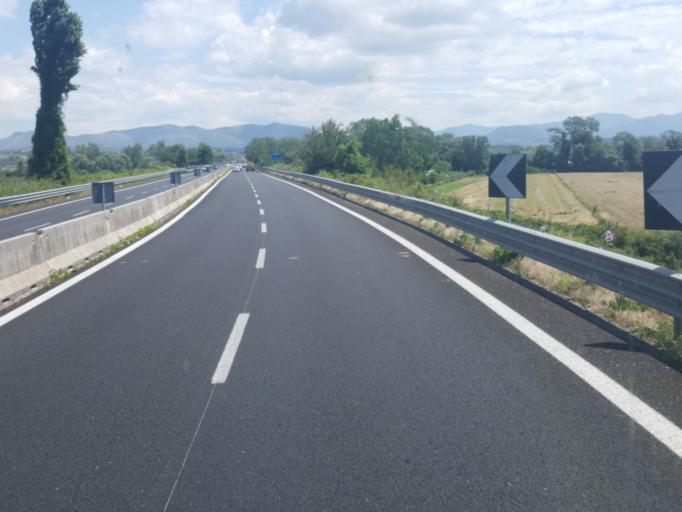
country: IT
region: Latium
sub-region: Citta metropolitana di Roma Capitale
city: Fiano Romano
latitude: 42.1500
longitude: 12.6313
